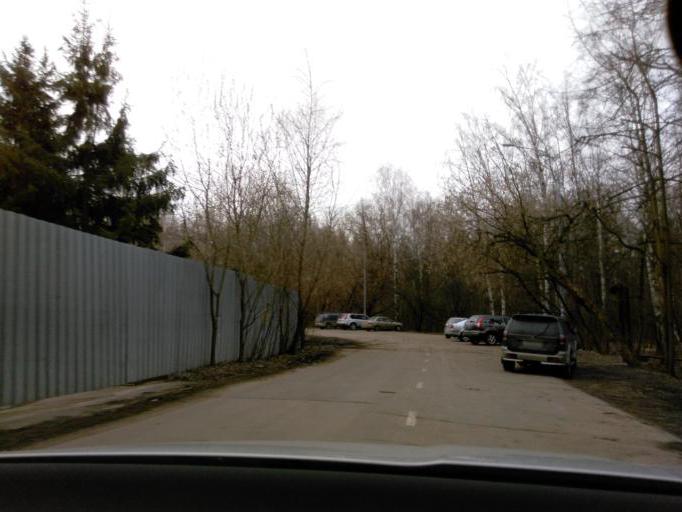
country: RU
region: Moskovskaya
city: Levoberezhnyy
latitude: 55.8270
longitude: 37.4775
